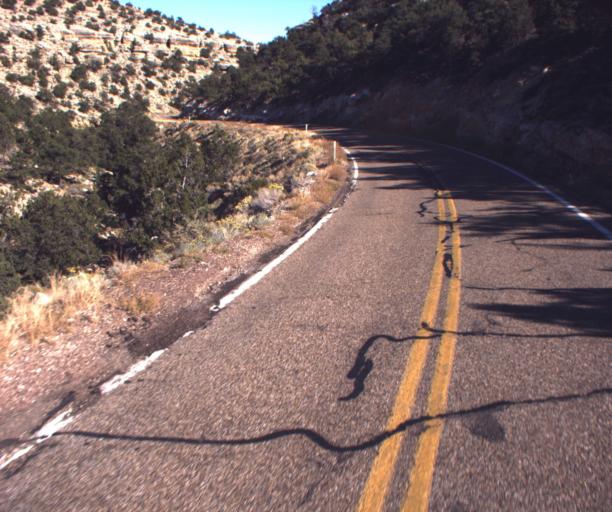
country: US
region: Arizona
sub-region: Coconino County
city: Fredonia
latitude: 36.7255
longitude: -112.0856
